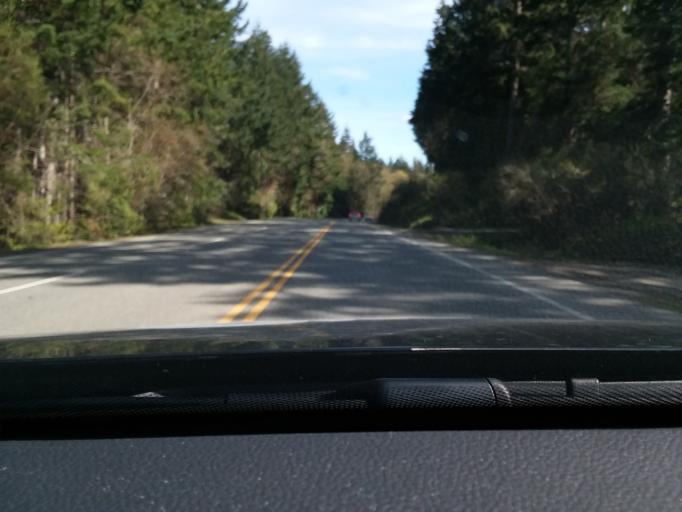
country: CA
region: British Columbia
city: North Saanich
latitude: 48.8518
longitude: -123.4577
